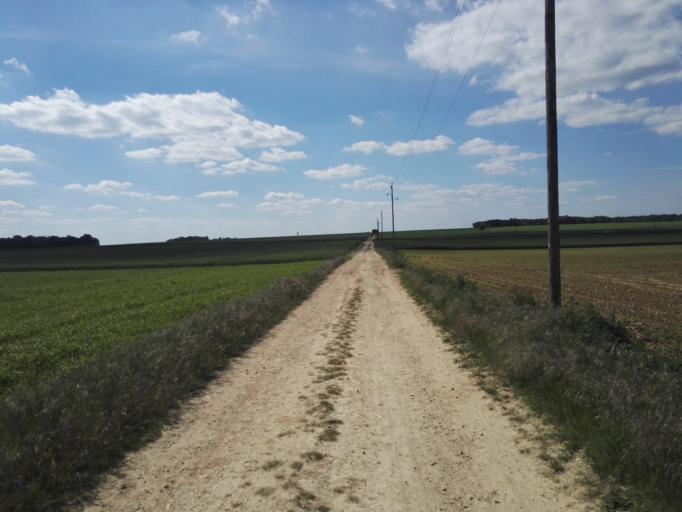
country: FR
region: Haute-Normandie
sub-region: Departement de l'Eure
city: Pacy-sur-Eure
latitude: 48.9964
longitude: 1.3490
